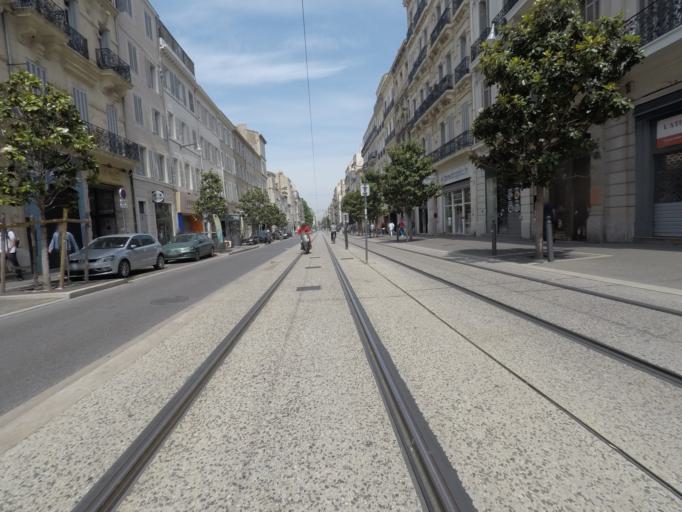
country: FR
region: Provence-Alpes-Cote d'Azur
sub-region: Departement des Bouches-du-Rhone
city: Marseille 06
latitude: 43.2880
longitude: 5.3826
